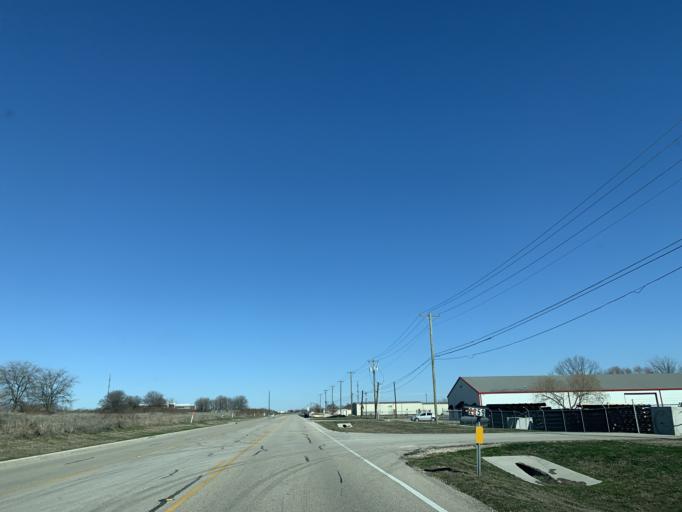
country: US
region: Texas
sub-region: Williamson County
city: Hutto
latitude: 30.5460
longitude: -97.5731
